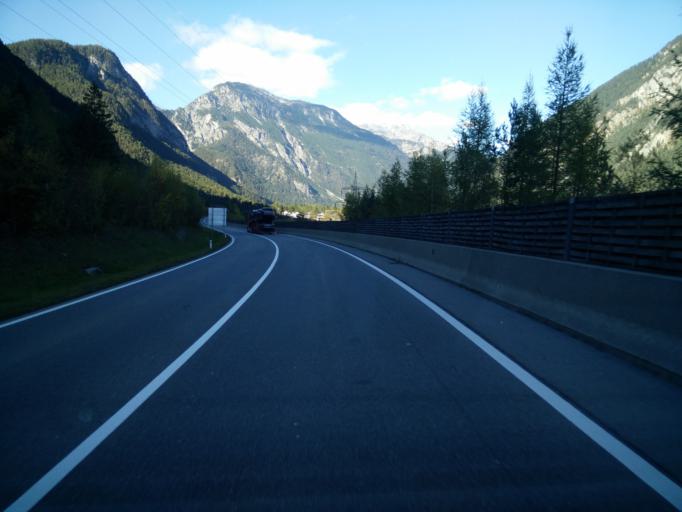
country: AT
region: Tyrol
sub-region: Politischer Bezirk Imst
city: Nassereith
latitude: 47.3114
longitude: 10.8348
